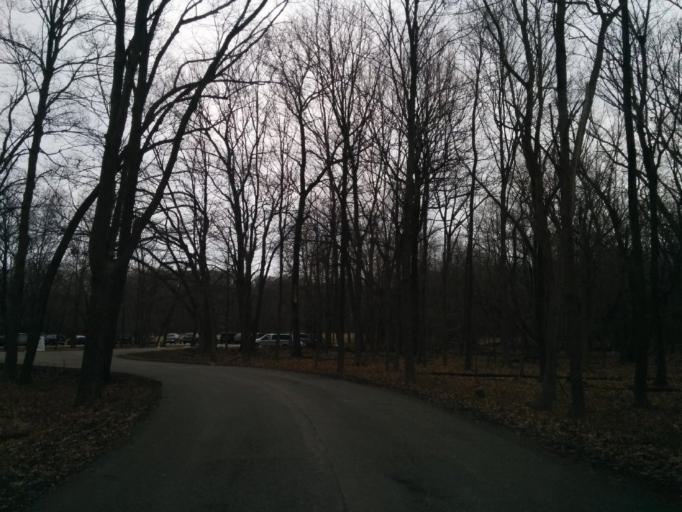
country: US
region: Illinois
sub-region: Cook County
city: Prospect Heights
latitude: 42.0901
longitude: -87.8836
